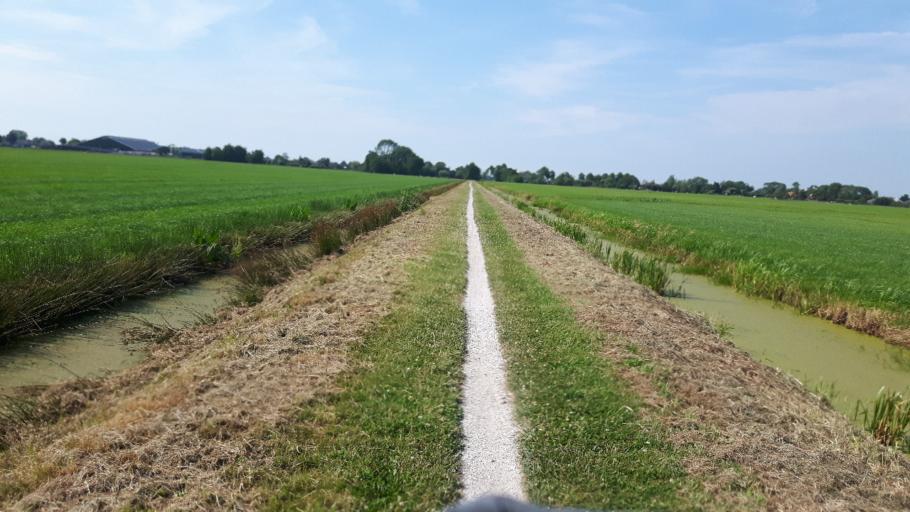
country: NL
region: Utrecht
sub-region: Gemeente Oudewater
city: Oudewater
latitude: 51.9819
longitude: 4.8867
